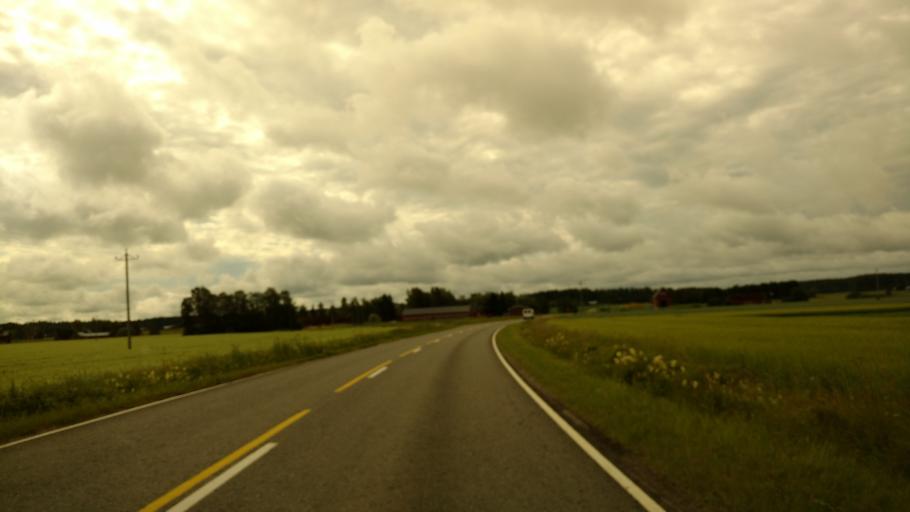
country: FI
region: Varsinais-Suomi
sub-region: Salo
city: Kuusjoki
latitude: 60.5182
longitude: 23.1784
